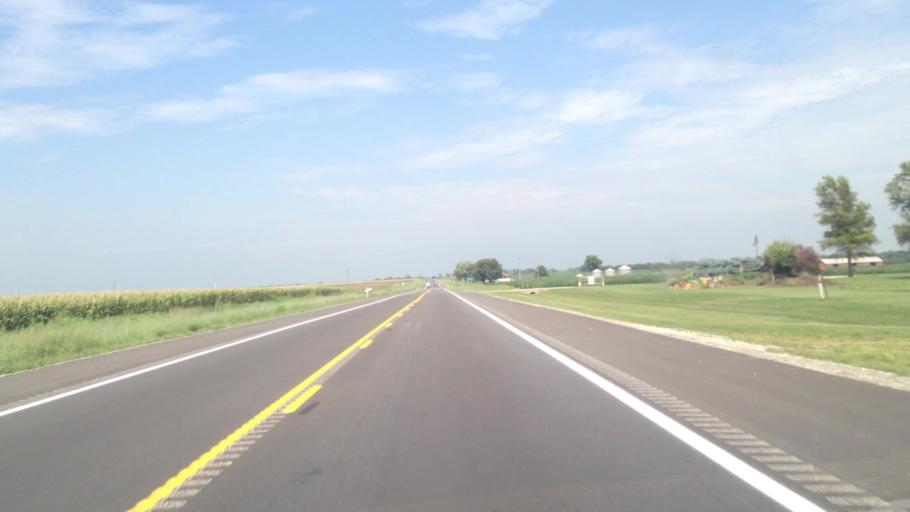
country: US
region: Kansas
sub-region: Anderson County
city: Garnett
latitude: 38.4303
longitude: -95.2486
